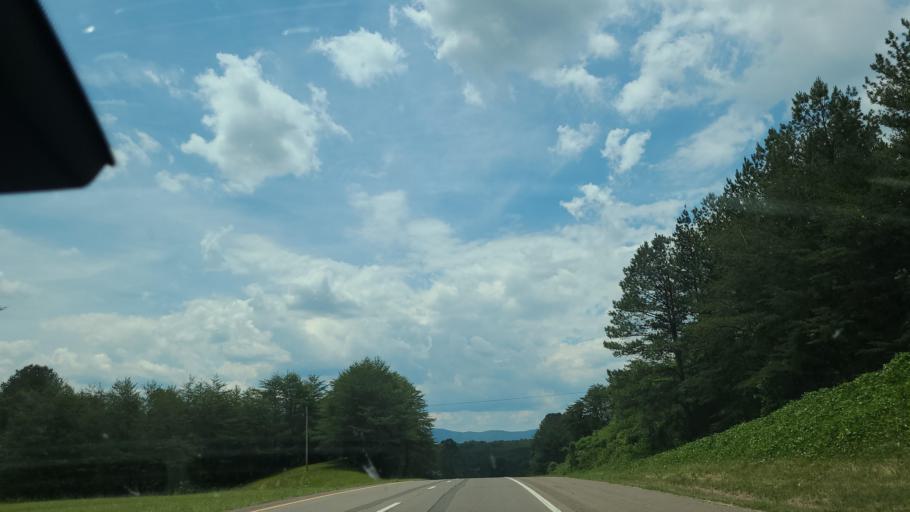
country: US
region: Georgia
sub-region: Fannin County
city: McCaysville
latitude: 35.0239
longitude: -84.3631
